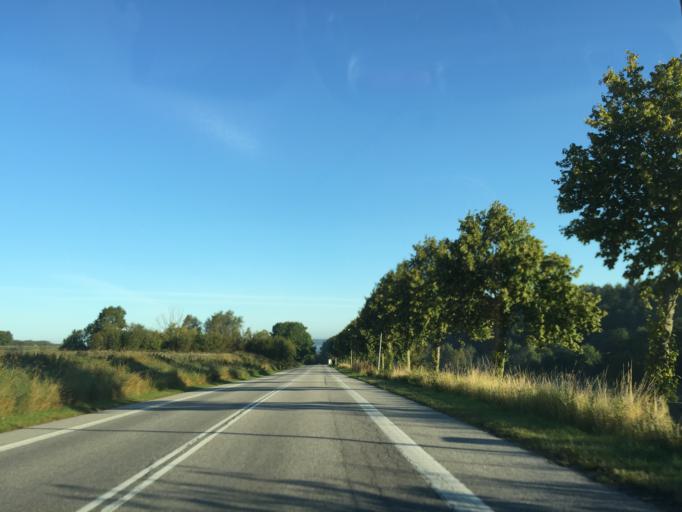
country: DK
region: Central Jutland
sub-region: Viborg Kommune
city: Bjerringbro
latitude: 56.3583
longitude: 9.6671
